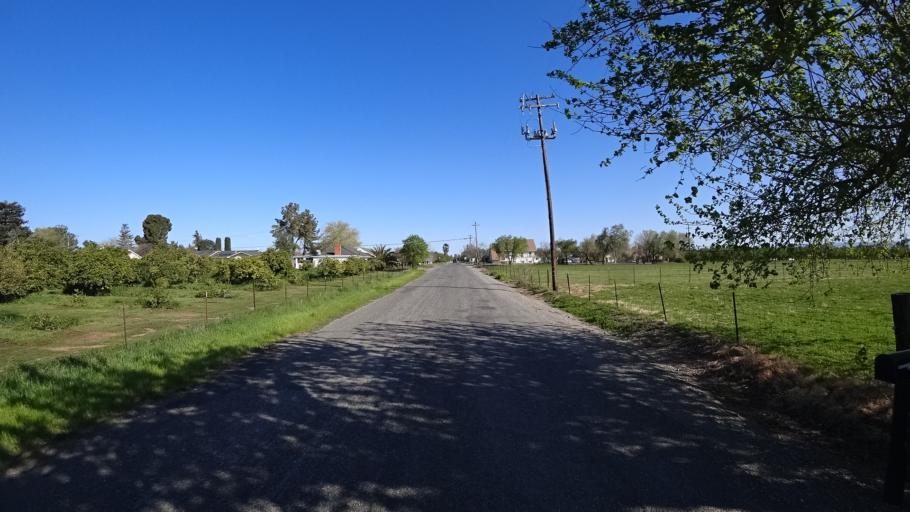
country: US
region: California
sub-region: Glenn County
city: Hamilton City
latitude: 39.7959
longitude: -122.0665
